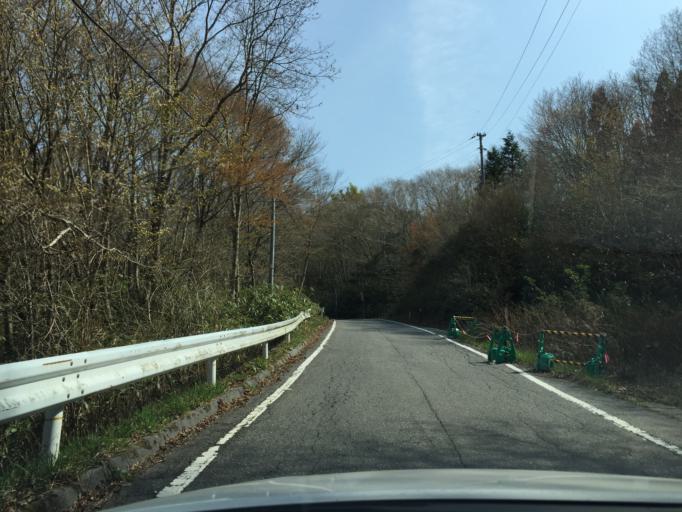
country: JP
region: Fukushima
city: Iwaki
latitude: 37.2162
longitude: 140.8495
